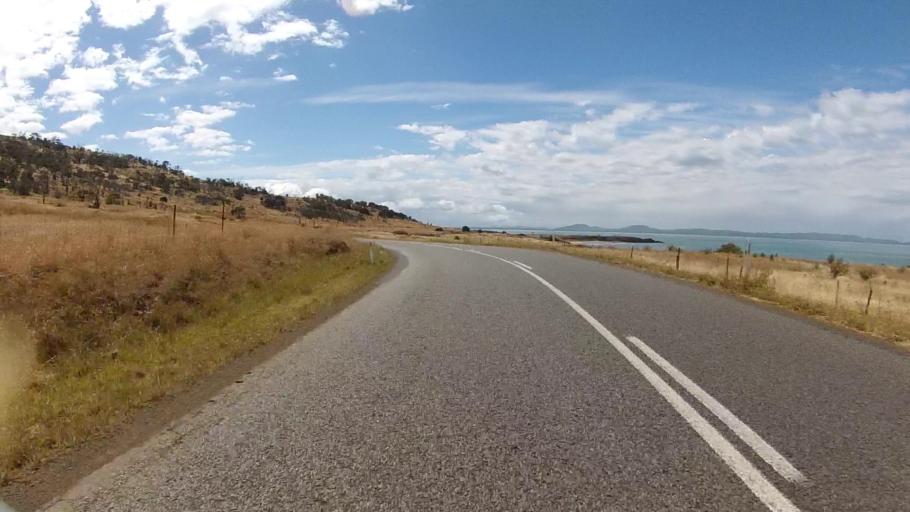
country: AU
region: Tasmania
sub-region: Sorell
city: Sorell
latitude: -42.1782
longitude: 148.0680
